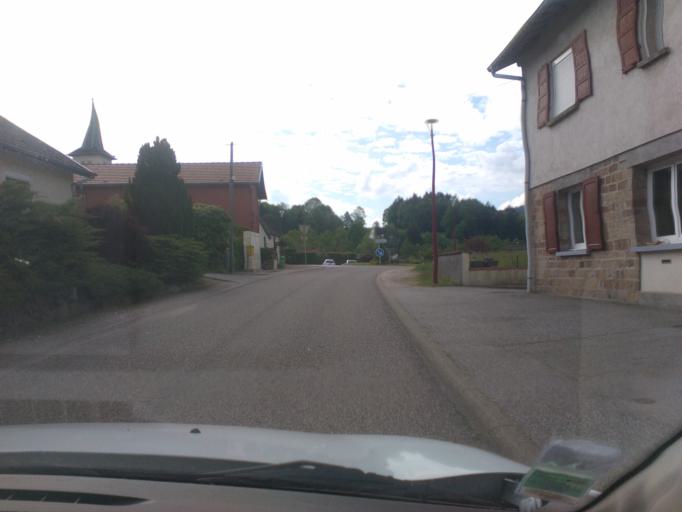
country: FR
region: Lorraine
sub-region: Departement des Vosges
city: Le Tholy
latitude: 48.1203
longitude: 6.7305
